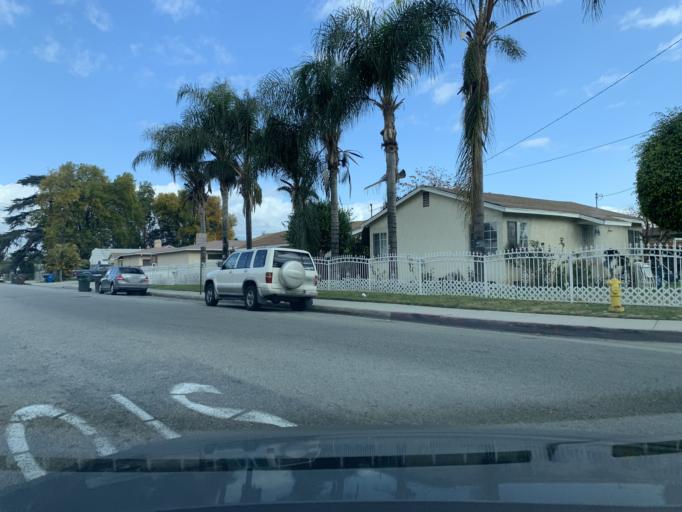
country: US
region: California
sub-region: Los Angeles County
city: South El Monte
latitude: 34.0640
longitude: -118.0479
